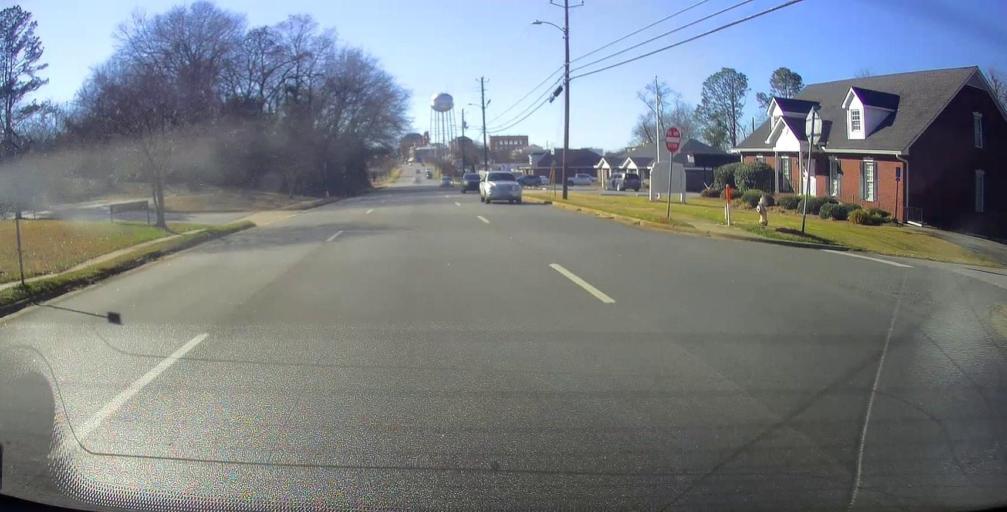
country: US
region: Georgia
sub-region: Sumter County
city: Americus
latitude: 32.0719
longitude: -84.2273
